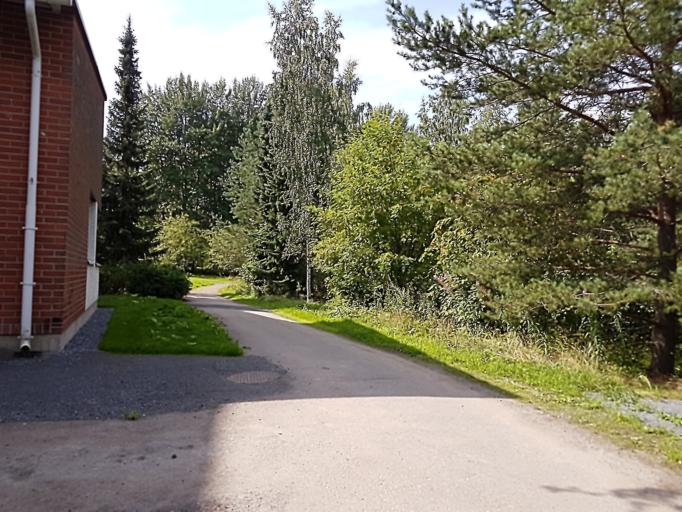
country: FI
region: Pirkanmaa
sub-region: Etelae-Pirkanmaa
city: Valkeakoski
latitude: 61.2543
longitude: 24.0419
